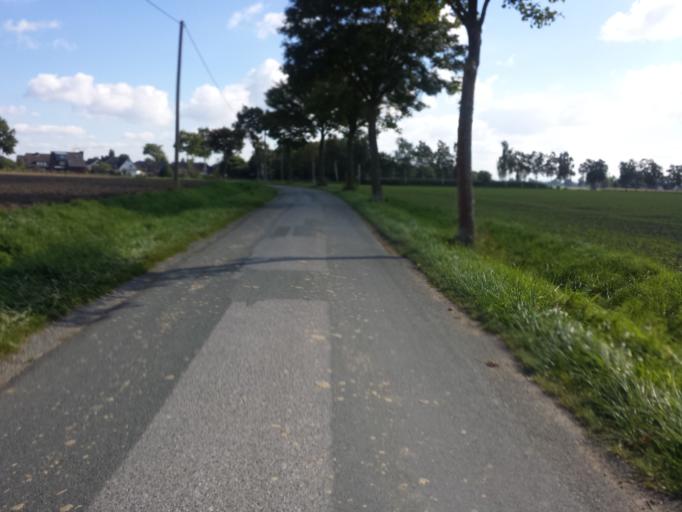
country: DE
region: North Rhine-Westphalia
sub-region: Regierungsbezirk Detmold
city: Langenberg
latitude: 51.7662
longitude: 8.3062
